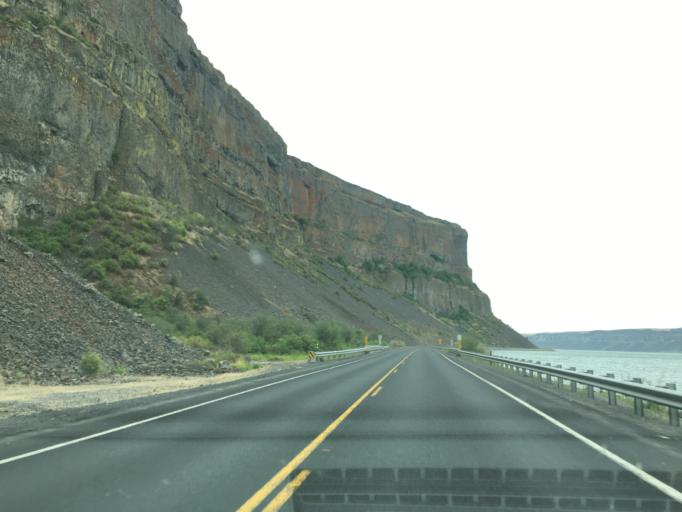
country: US
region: Washington
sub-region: Okanogan County
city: Coulee Dam
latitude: 47.8197
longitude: -119.1490
